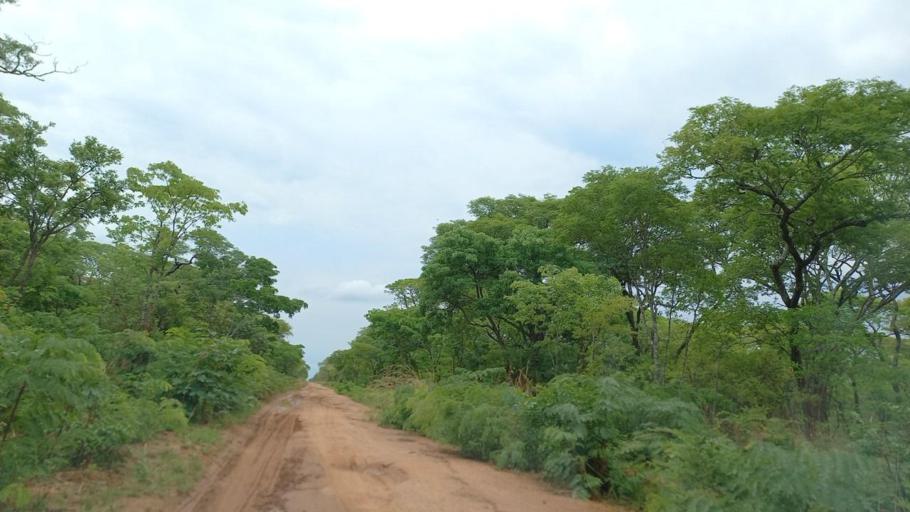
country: ZM
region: North-Western
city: Kalengwa
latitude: -13.6066
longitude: 24.9750
